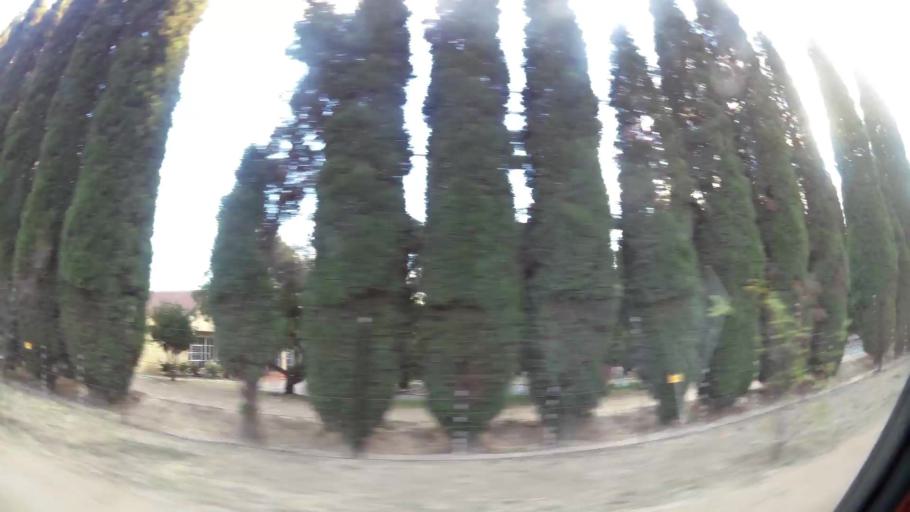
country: ZA
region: Gauteng
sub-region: City of Johannesburg Metropolitan Municipality
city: Midrand
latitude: -26.0017
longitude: 28.1515
